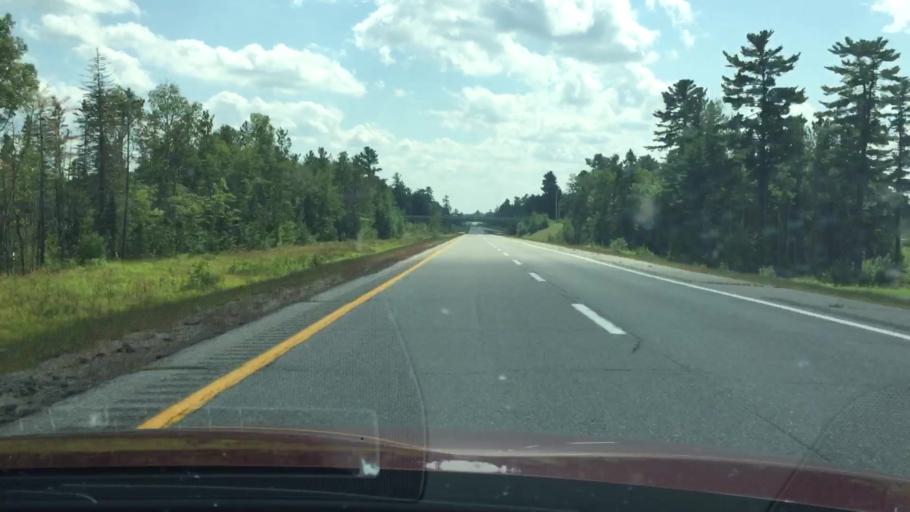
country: US
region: Maine
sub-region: Penobscot County
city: Lincoln
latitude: 45.3789
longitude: -68.6055
